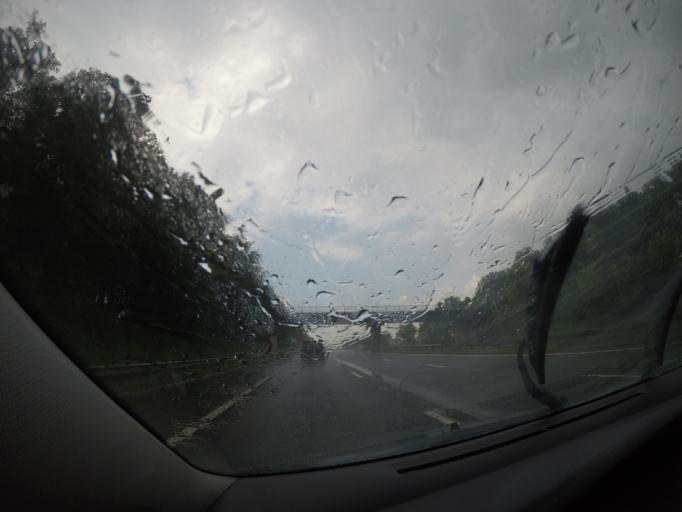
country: GB
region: England
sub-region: Cumbria
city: Penrith
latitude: 54.7224
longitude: -2.8004
